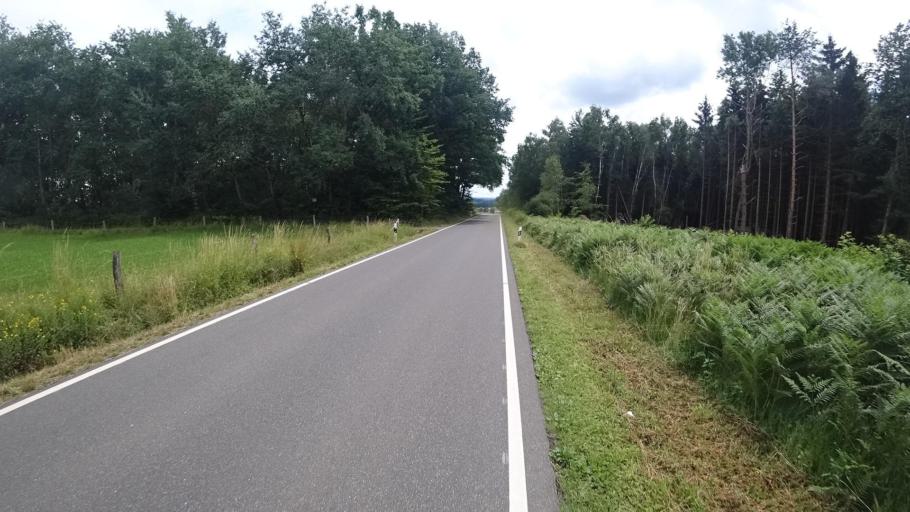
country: DE
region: Rheinland-Pfalz
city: Fiersbach
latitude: 50.6983
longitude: 7.4858
